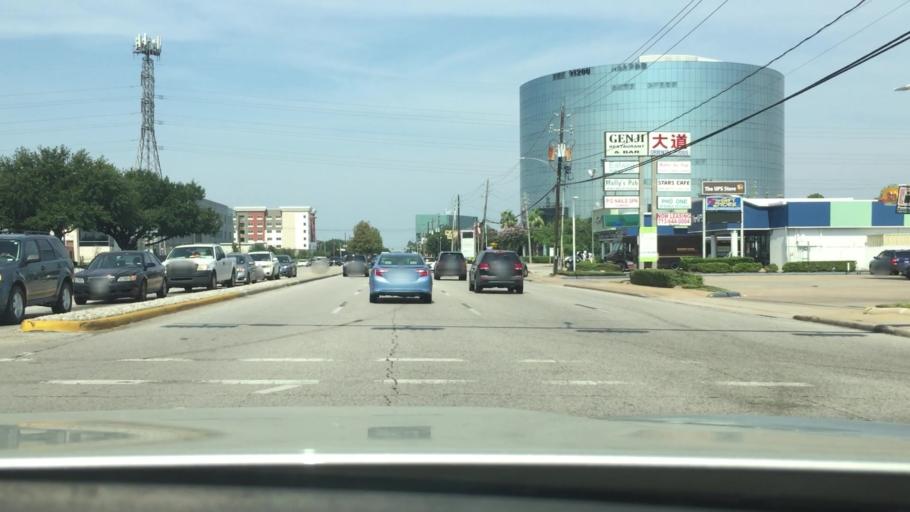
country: US
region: Texas
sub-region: Harris County
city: Bunker Hill Village
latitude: 29.7368
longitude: -95.5719
